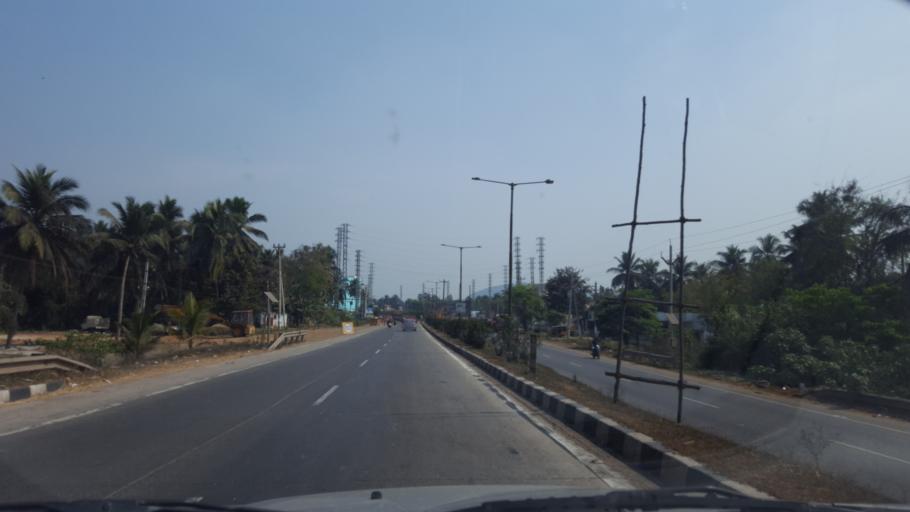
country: IN
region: Andhra Pradesh
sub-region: Vishakhapatnam
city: Anakapalle
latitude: 17.6777
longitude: 82.9946
